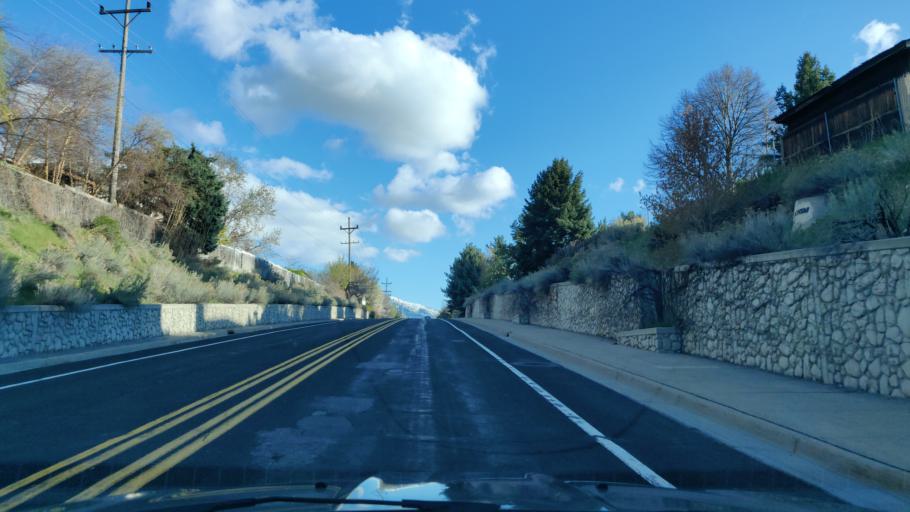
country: US
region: Utah
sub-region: Salt Lake County
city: Cottonwood Heights
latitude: 40.6277
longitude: -111.8077
